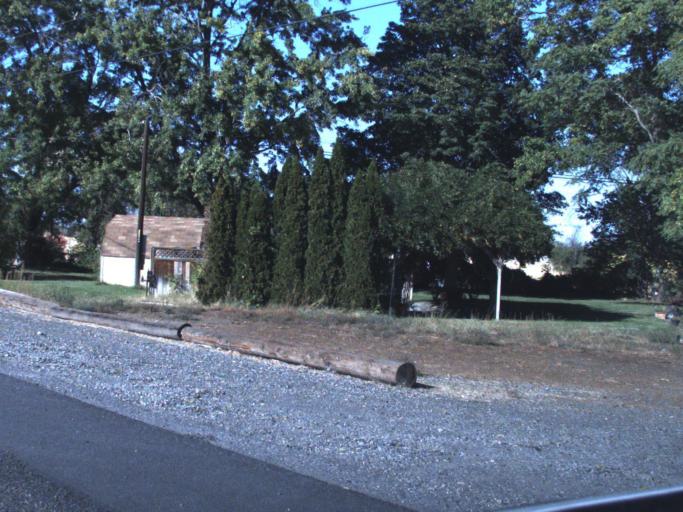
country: US
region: Washington
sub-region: Benton County
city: Finley
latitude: 46.1830
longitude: -119.0688
